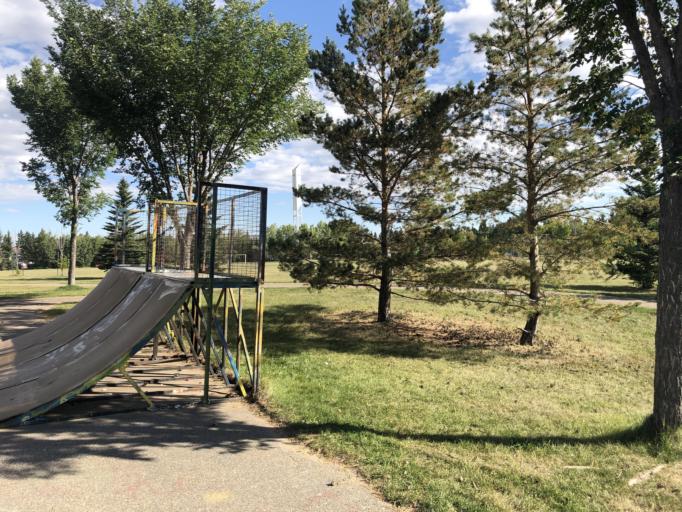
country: CA
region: Alberta
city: Edmonton
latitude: 53.4815
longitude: -113.5815
